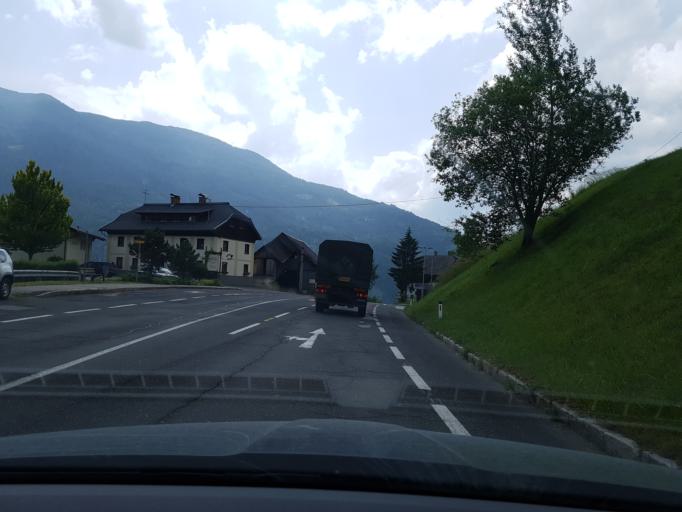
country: AT
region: Carinthia
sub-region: Politischer Bezirk Villach Land
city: Feld am See
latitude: 46.7964
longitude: 13.7383
